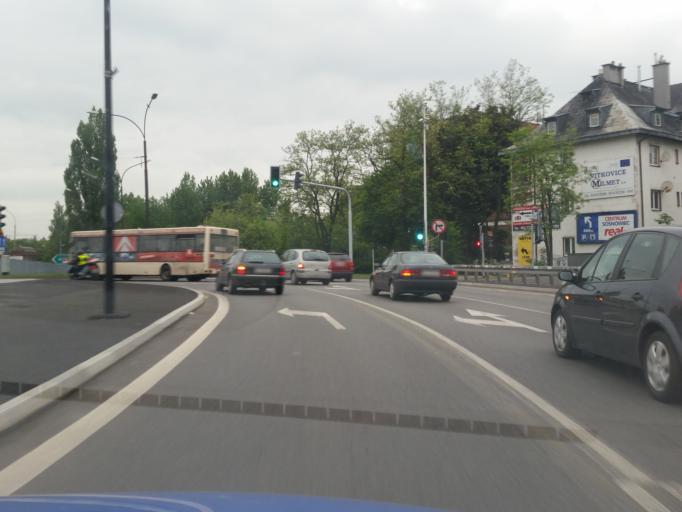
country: PL
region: Silesian Voivodeship
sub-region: Sosnowiec
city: Sosnowiec
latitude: 50.2862
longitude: 19.1041
